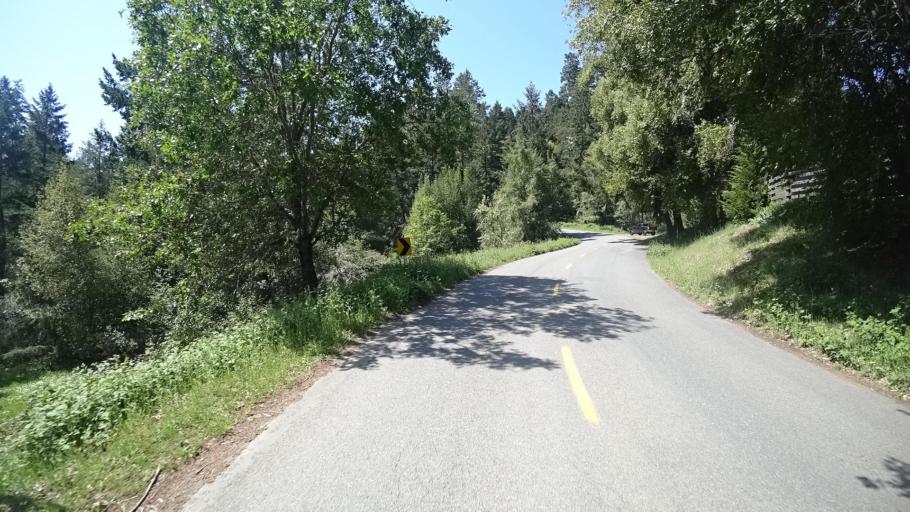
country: US
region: California
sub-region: Humboldt County
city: Redway
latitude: 40.1507
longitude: -123.6251
